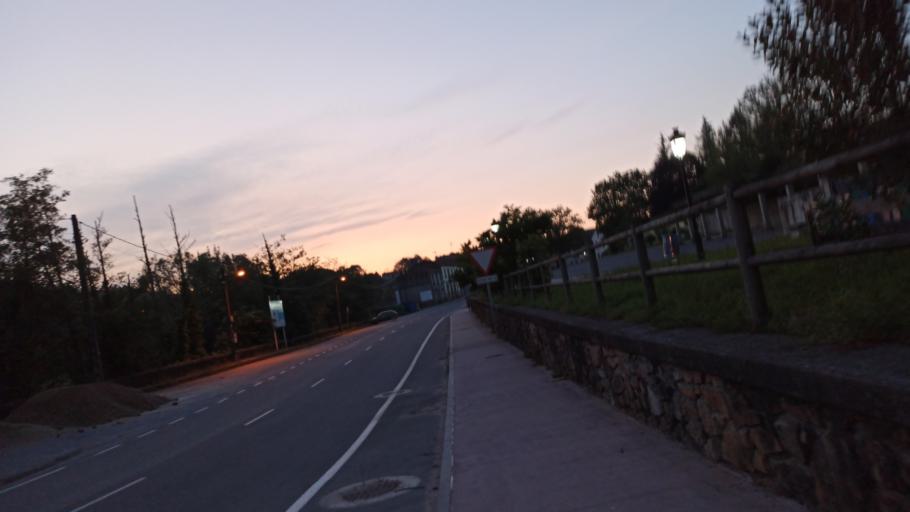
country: ES
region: Galicia
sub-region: Provincia da Coruna
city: Negreira
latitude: 42.9059
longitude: -8.7384
